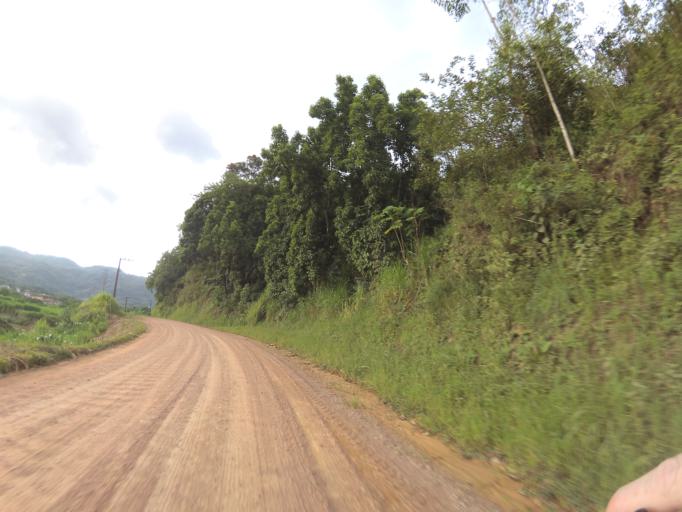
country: BR
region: Santa Catarina
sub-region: Pomerode
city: Pomerode
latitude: -26.7623
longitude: -49.1647
